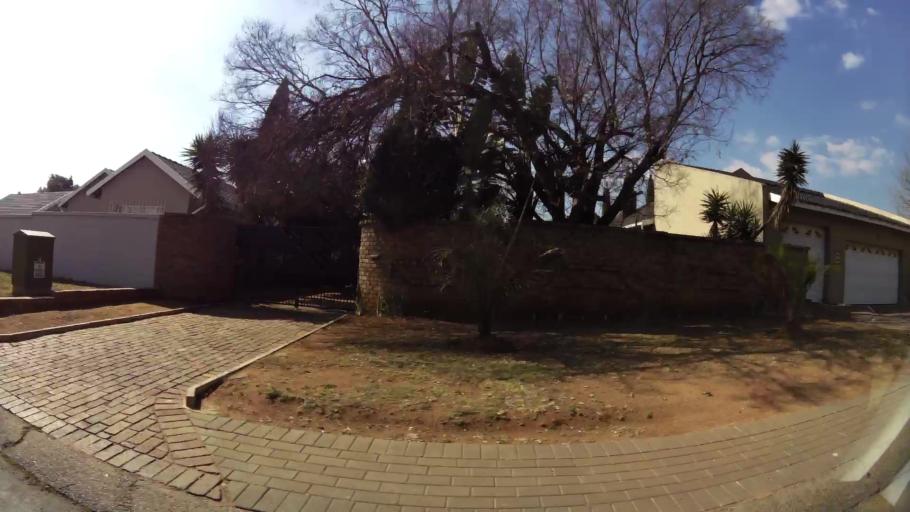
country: ZA
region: Gauteng
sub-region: Ekurhuleni Metropolitan Municipality
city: Tembisa
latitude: -26.0805
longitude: 28.2566
